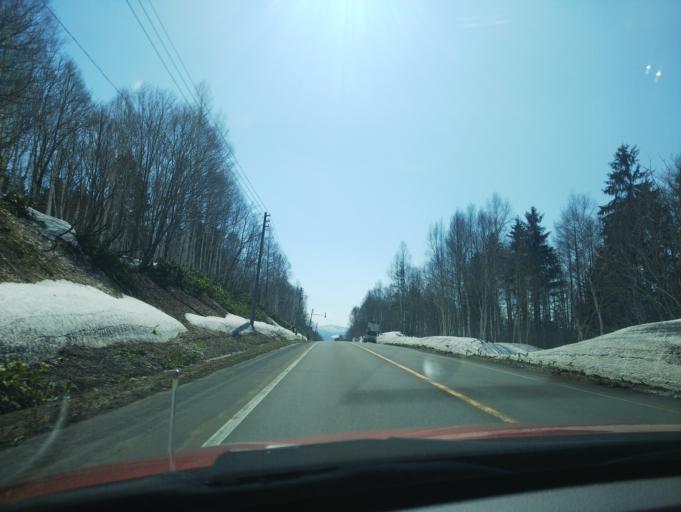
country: JP
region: Hokkaido
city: Nayoro
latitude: 44.6419
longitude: 142.2696
